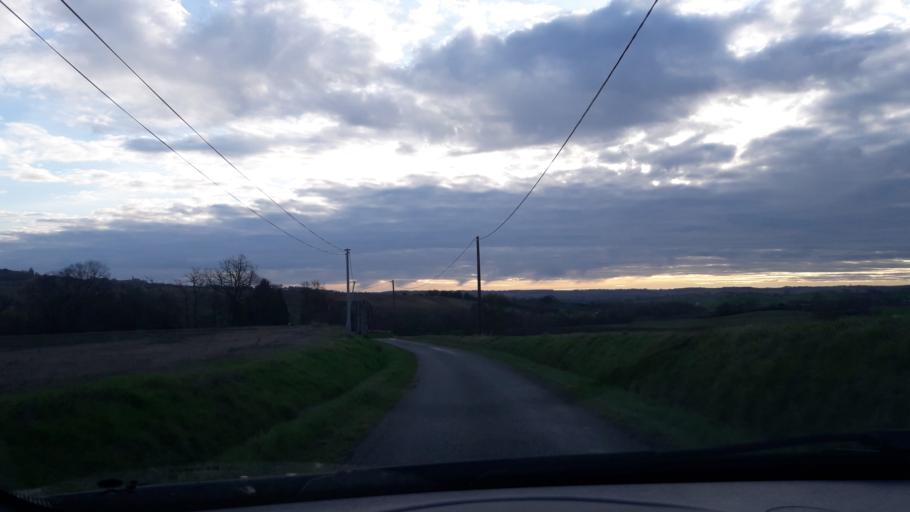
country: FR
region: Midi-Pyrenees
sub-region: Departement du Gers
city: Pujaudran
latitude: 43.6659
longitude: 1.0874
